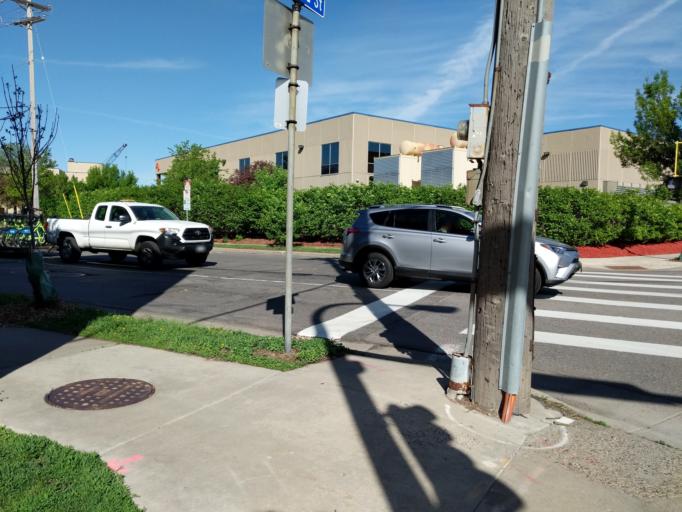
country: US
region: Minnesota
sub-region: Hennepin County
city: Minneapolis
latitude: 44.9910
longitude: -93.2794
